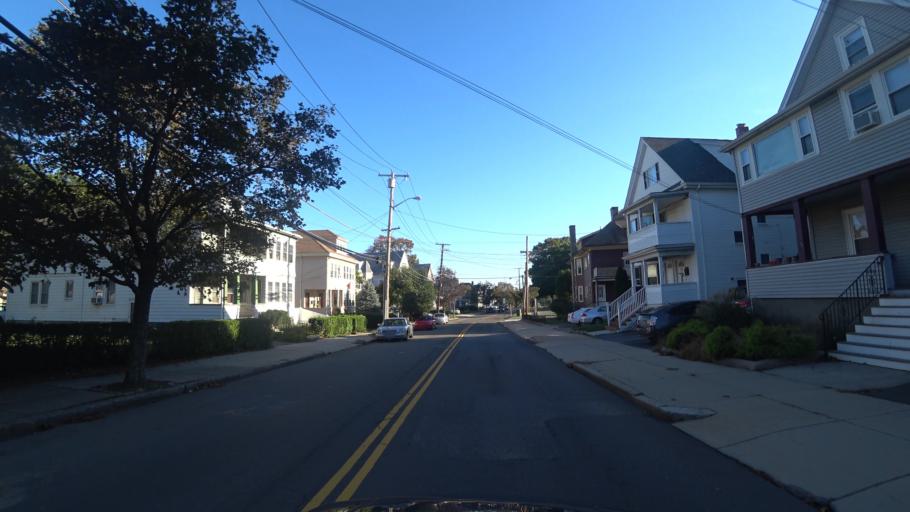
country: US
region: Massachusetts
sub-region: Middlesex County
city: Malden
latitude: 42.4326
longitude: -71.0821
